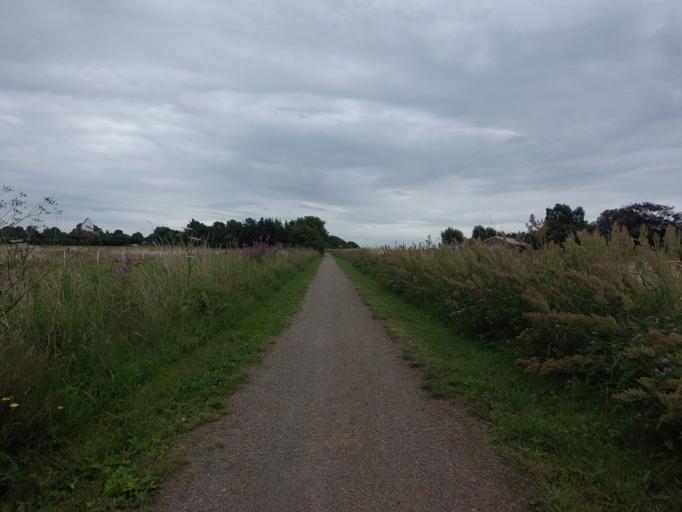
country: DK
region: North Denmark
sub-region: Alborg Kommune
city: Vadum
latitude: 57.1135
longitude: 9.8797
